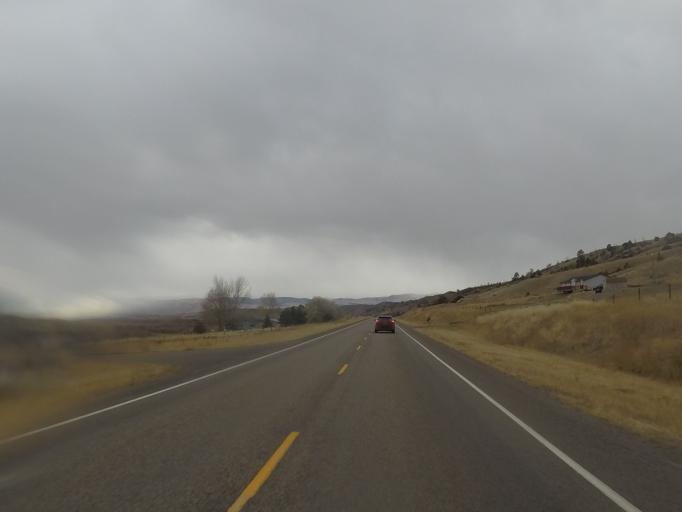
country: US
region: Montana
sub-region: Broadwater County
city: Townsend
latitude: 46.3286
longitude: -111.3625
